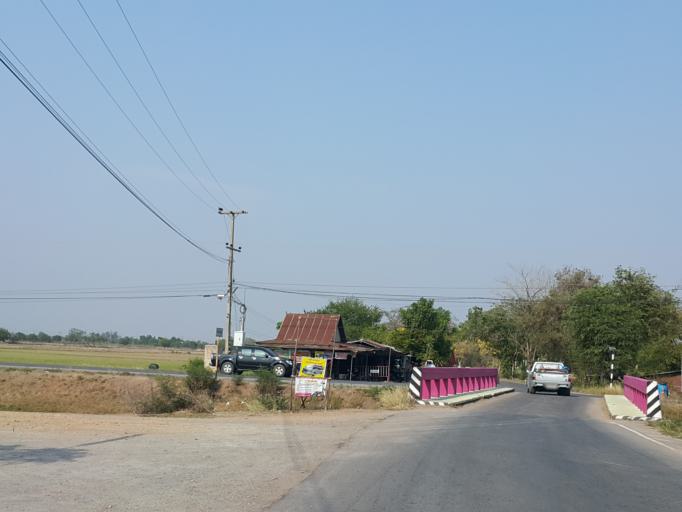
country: TH
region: Suphan Buri
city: Sam Chuk
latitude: 14.7491
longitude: 100.0565
